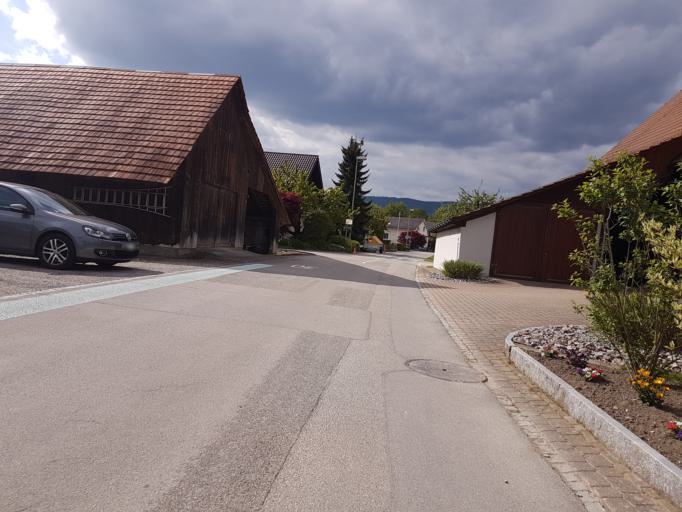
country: CH
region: Bern
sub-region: Biel/Bienne District
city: Meinisberg
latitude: 47.1428
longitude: 7.3697
